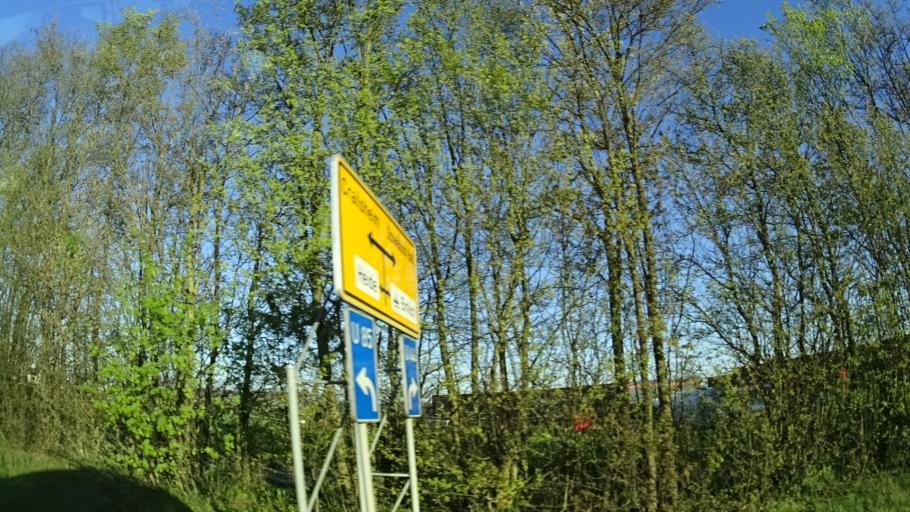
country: DE
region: Baden-Wuerttemberg
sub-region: Regierungsbezirk Stuttgart
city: Wolpertshausen
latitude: 49.1708
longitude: 9.8613
